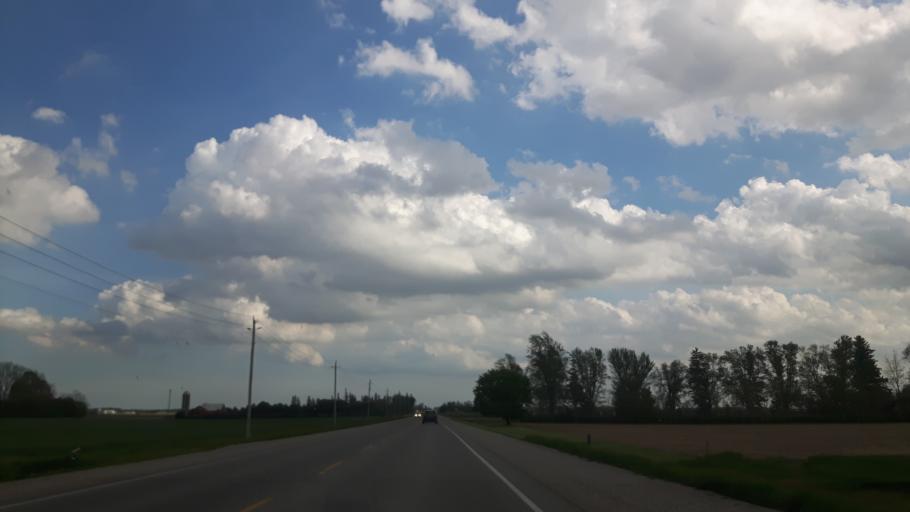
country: CA
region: Ontario
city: South Huron
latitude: 43.3840
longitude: -81.4882
